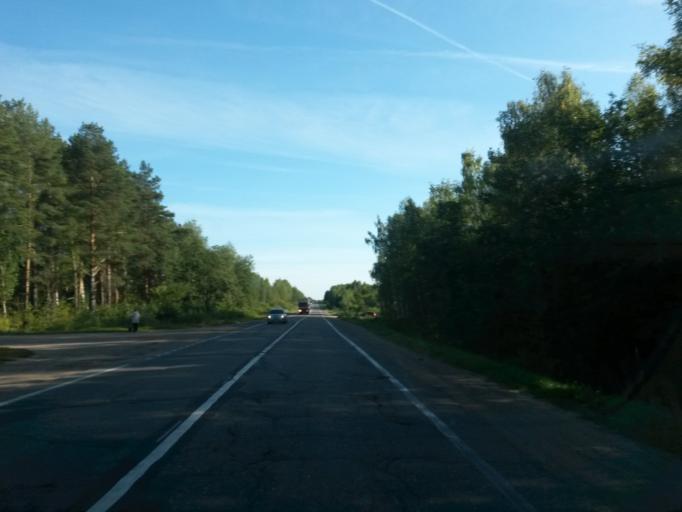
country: RU
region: Jaroslavl
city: Gavrilov-Yam
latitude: 57.3697
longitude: 39.9075
